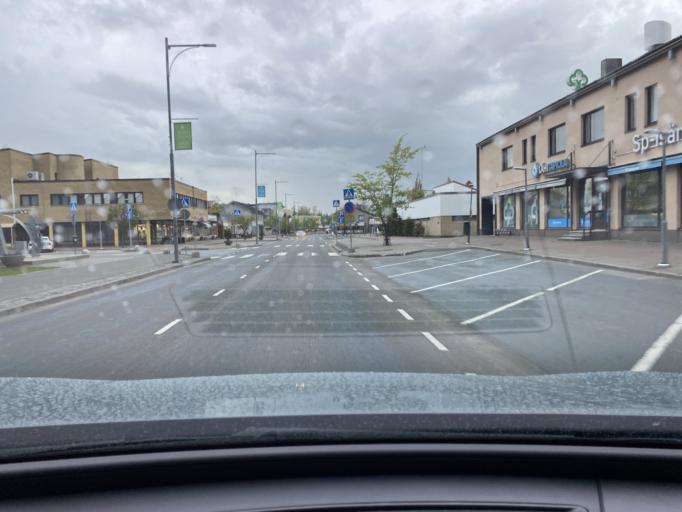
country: FI
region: Varsinais-Suomi
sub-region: Salo
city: Somero
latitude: 60.6290
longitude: 23.5143
